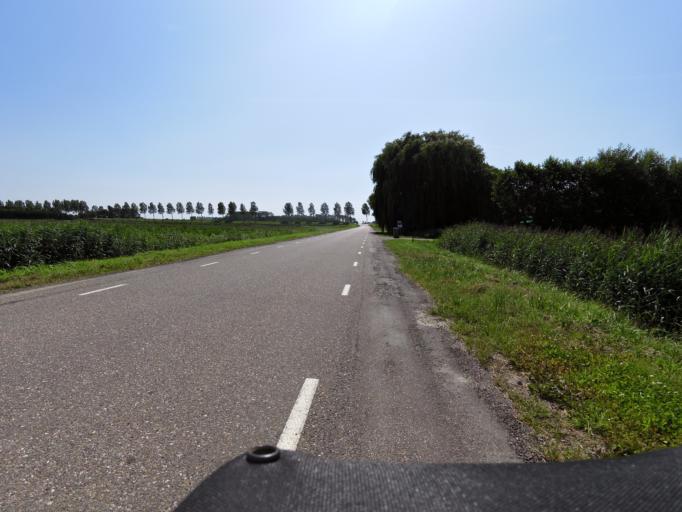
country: NL
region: South Holland
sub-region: Gemeente Goeree-Overflakkee
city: Middelharnis
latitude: 51.7219
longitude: 4.1423
